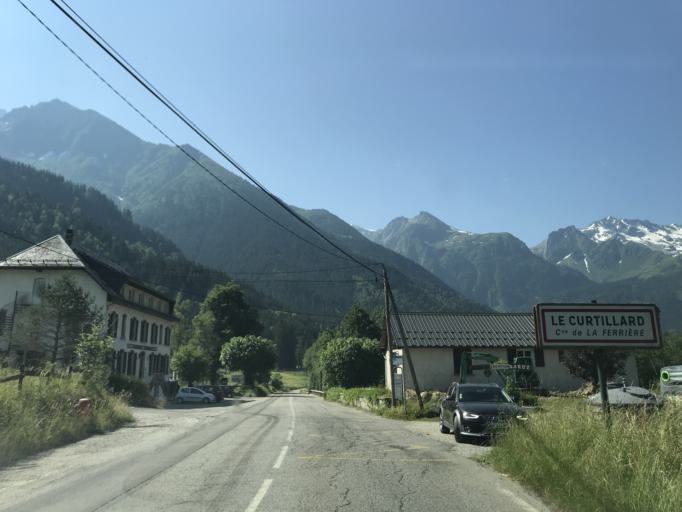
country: FR
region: Rhone-Alpes
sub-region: Departement de l'Isere
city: Theys
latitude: 45.3051
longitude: 6.0801
